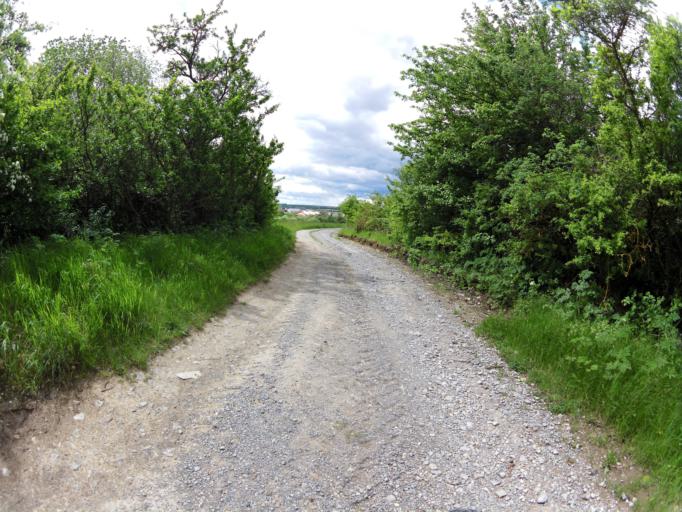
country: DE
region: Bavaria
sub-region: Regierungsbezirk Unterfranken
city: Volkach
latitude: 49.8712
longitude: 10.2372
